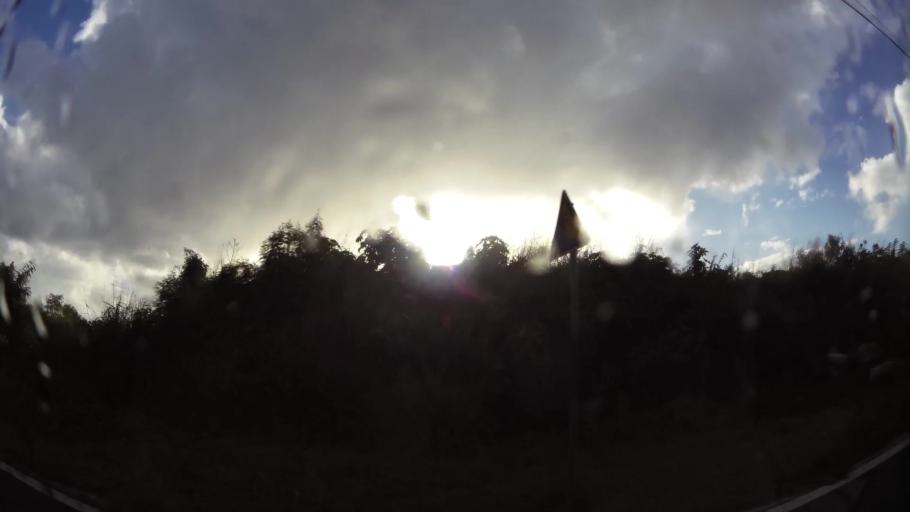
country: DM
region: Saint Paul
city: Mahaut
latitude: 15.3817
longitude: -61.4110
